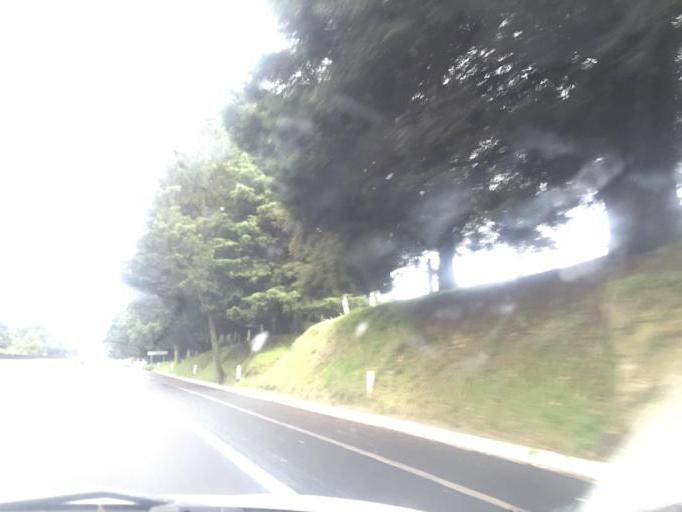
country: MX
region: Mexico City
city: Xochimilco
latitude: 19.1777
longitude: -99.1545
